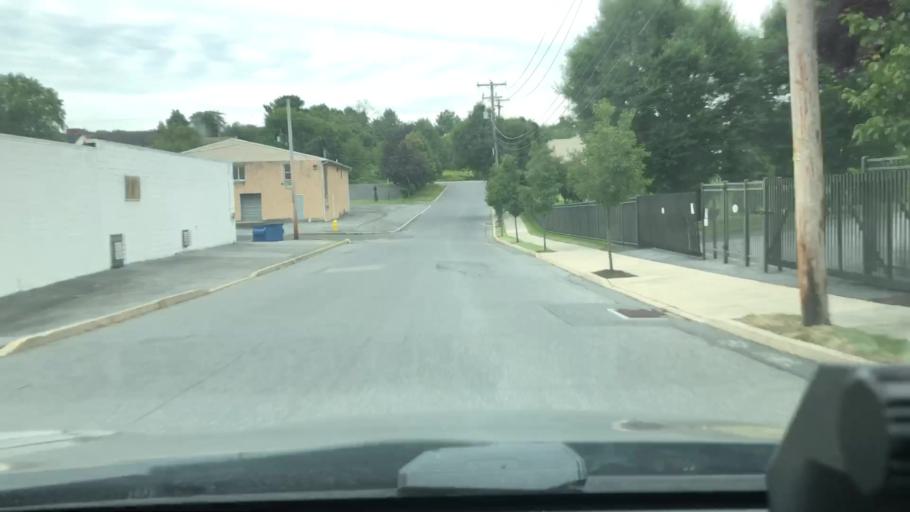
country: US
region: Pennsylvania
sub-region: Lehigh County
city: Fullerton
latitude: 40.6195
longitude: -75.4482
